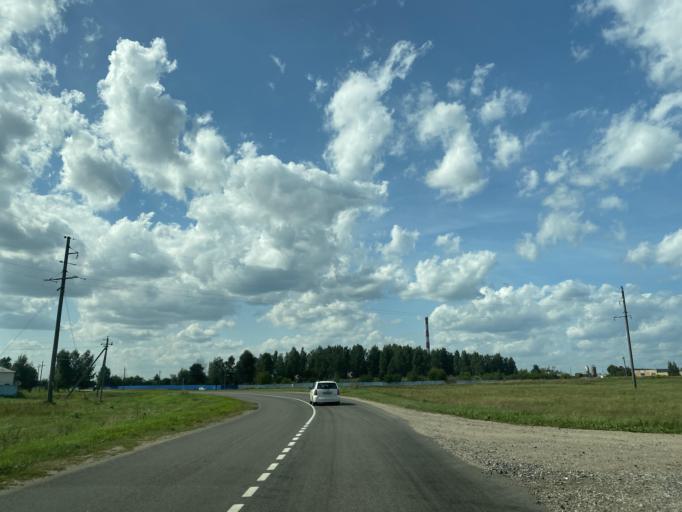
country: BY
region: Minsk
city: Horad Zhodzina
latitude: 54.0863
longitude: 28.3683
